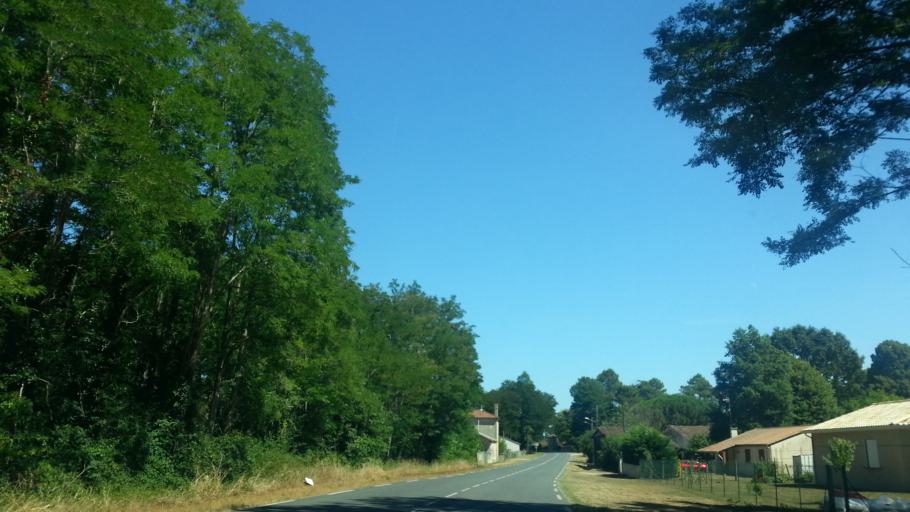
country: FR
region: Aquitaine
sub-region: Departement de la Gironde
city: Landiras
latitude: 44.5619
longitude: -0.3920
